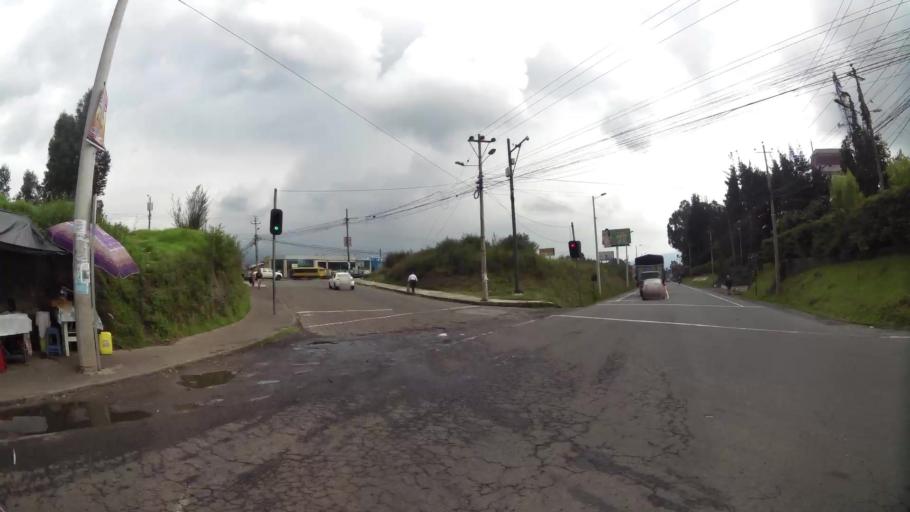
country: EC
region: Pichincha
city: Sangolqui
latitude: -0.3443
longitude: -78.4548
